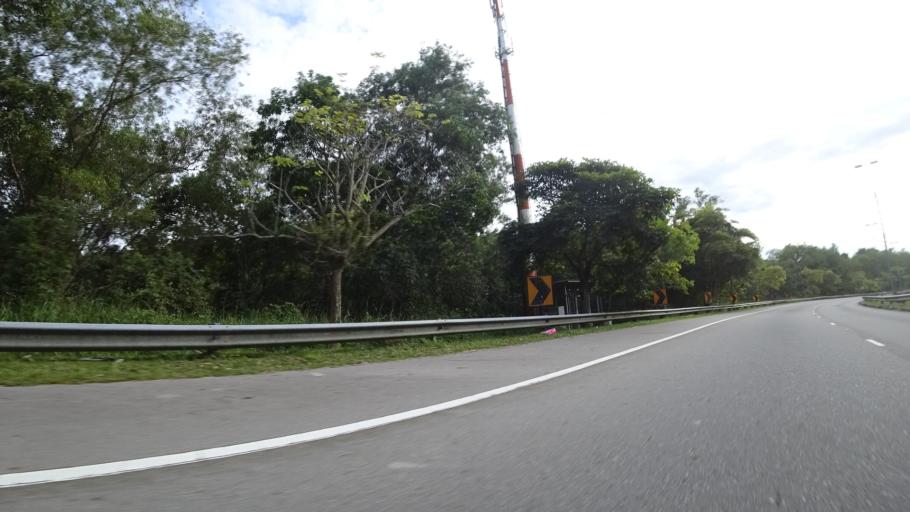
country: BN
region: Brunei and Muara
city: Bandar Seri Begawan
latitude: 4.9094
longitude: 114.9460
